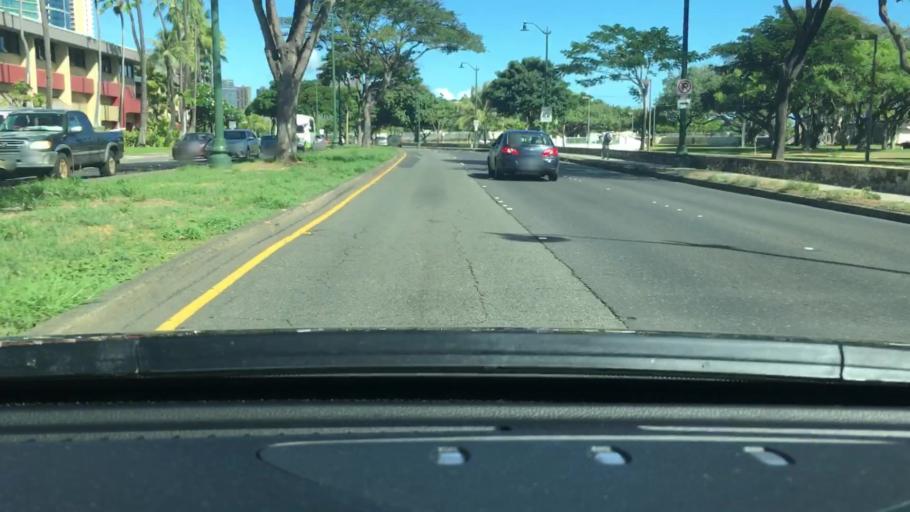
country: US
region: Hawaii
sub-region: Honolulu County
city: Honolulu
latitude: 21.2927
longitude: -157.8536
